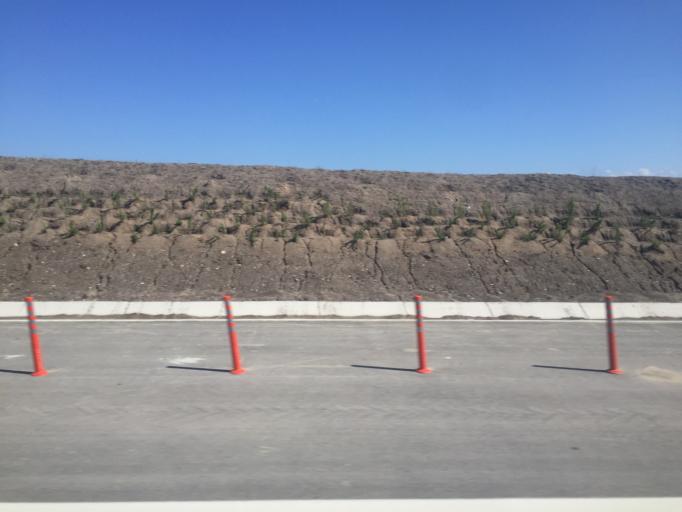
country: TR
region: Bursa
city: Mahmudiye
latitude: 40.2647
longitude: 28.6618
